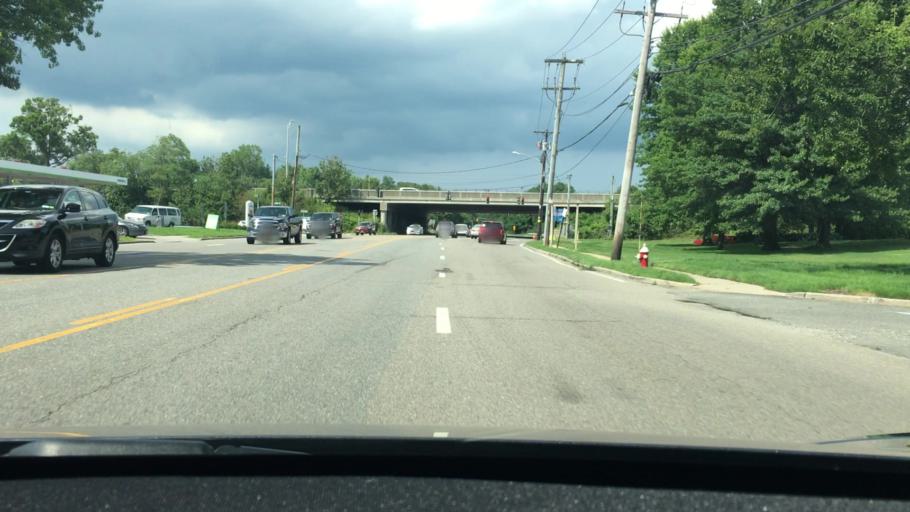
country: US
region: New York
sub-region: Nassau County
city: Old Bethpage
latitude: 40.7839
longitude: -73.4450
